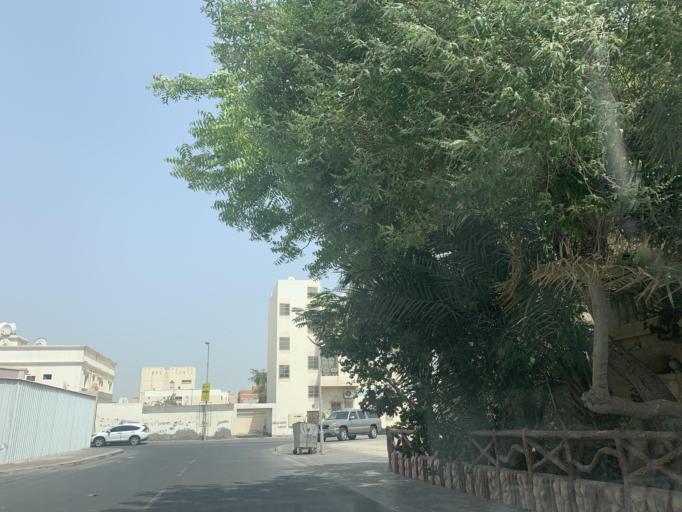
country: BH
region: Northern
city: Madinat `Isa
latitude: 26.1811
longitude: 50.5239
